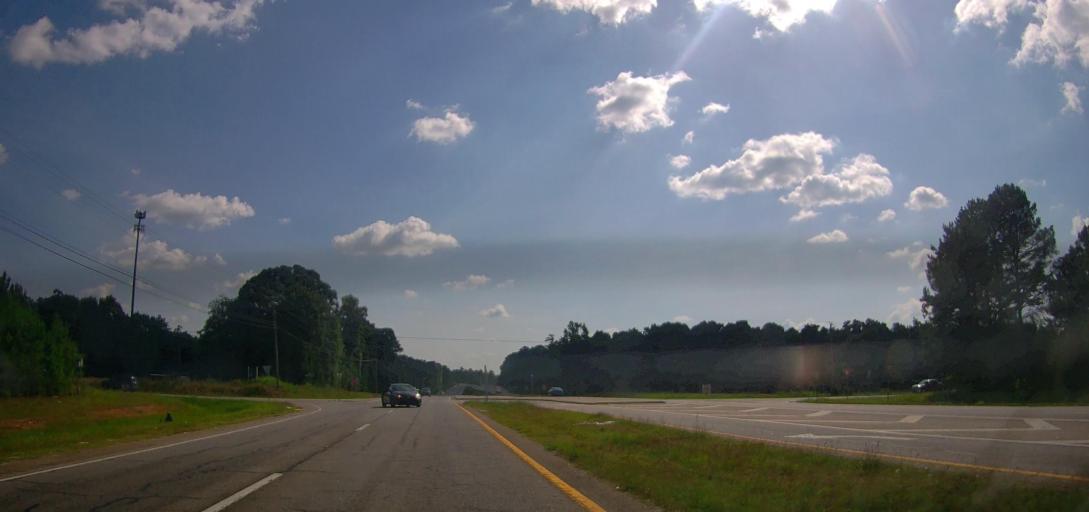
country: US
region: Georgia
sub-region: Henry County
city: Hampton
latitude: 33.4063
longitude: -84.2149
